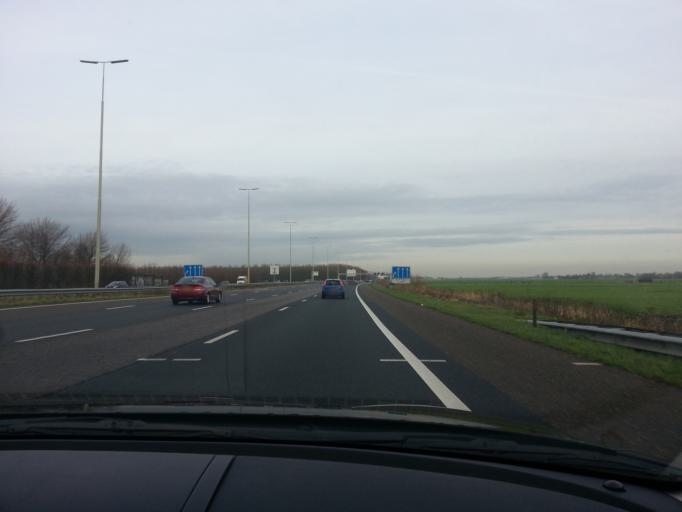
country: NL
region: South Holland
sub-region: Gemeente Leidschendam-Voorburg
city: Voorburg
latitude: 52.0819
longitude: 4.4105
